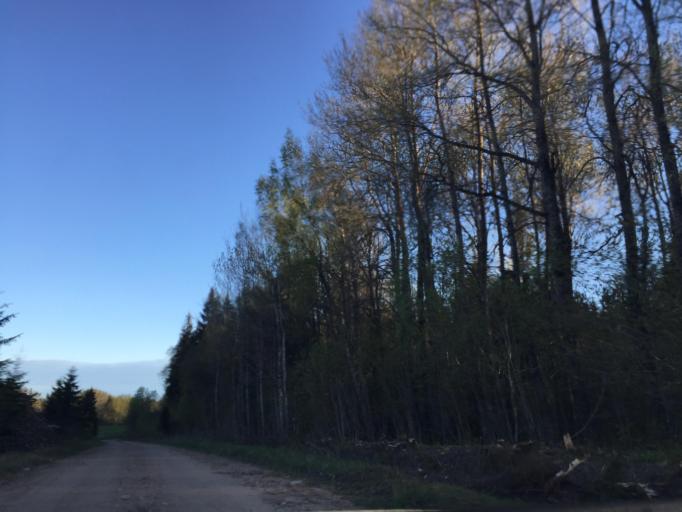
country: LV
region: Vecpiebalga
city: Vecpiebalga
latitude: 56.8688
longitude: 25.9705
